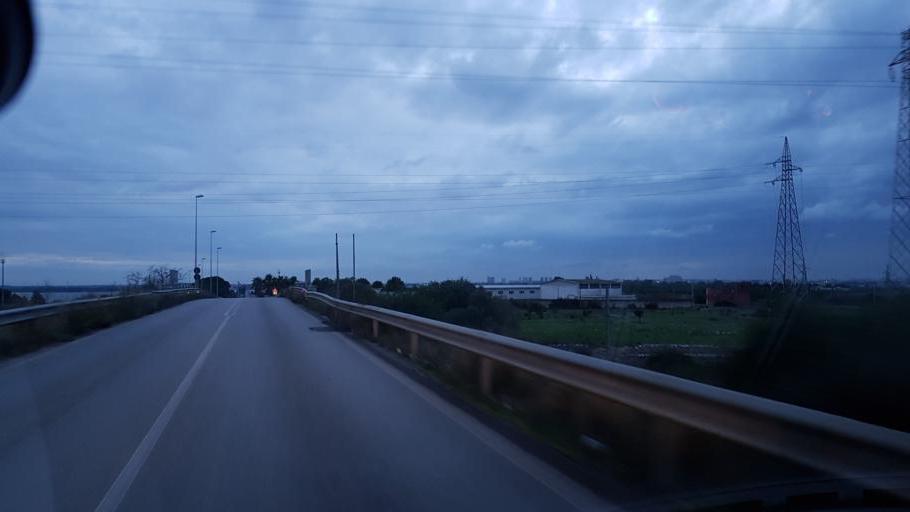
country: IT
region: Apulia
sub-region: Provincia di Taranto
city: Paolo VI
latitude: 40.5156
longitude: 17.2882
